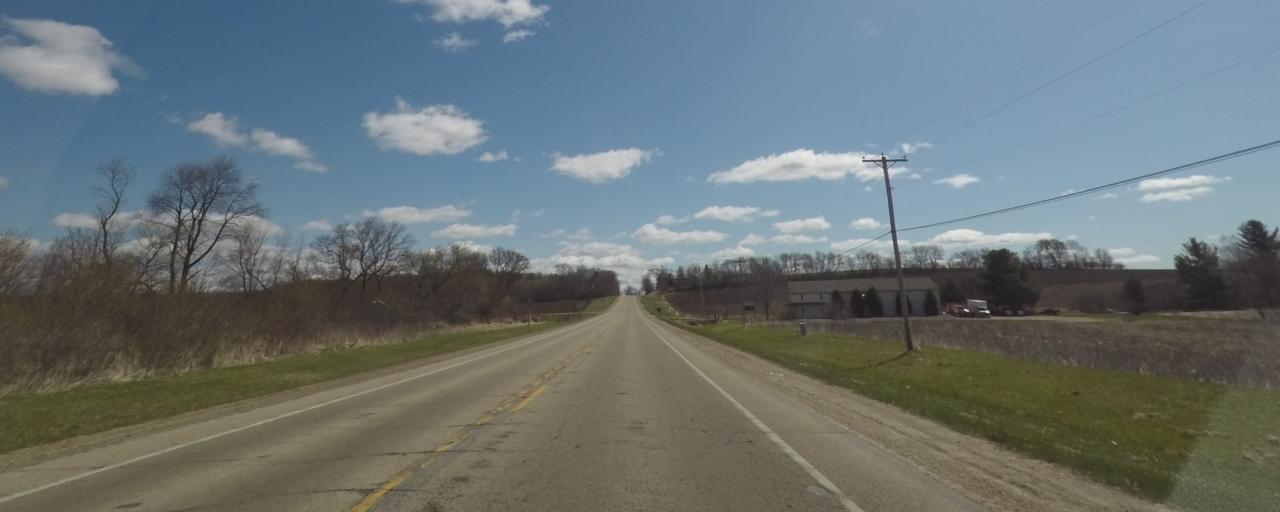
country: US
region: Wisconsin
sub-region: Dane County
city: Cottage Grove
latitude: 43.0901
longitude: -89.1918
